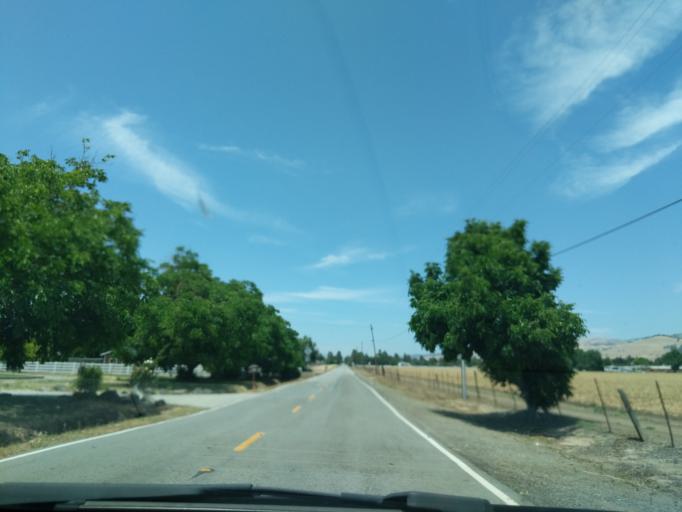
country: US
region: California
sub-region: Santa Clara County
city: Gilroy
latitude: 37.0514
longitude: -121.5638
